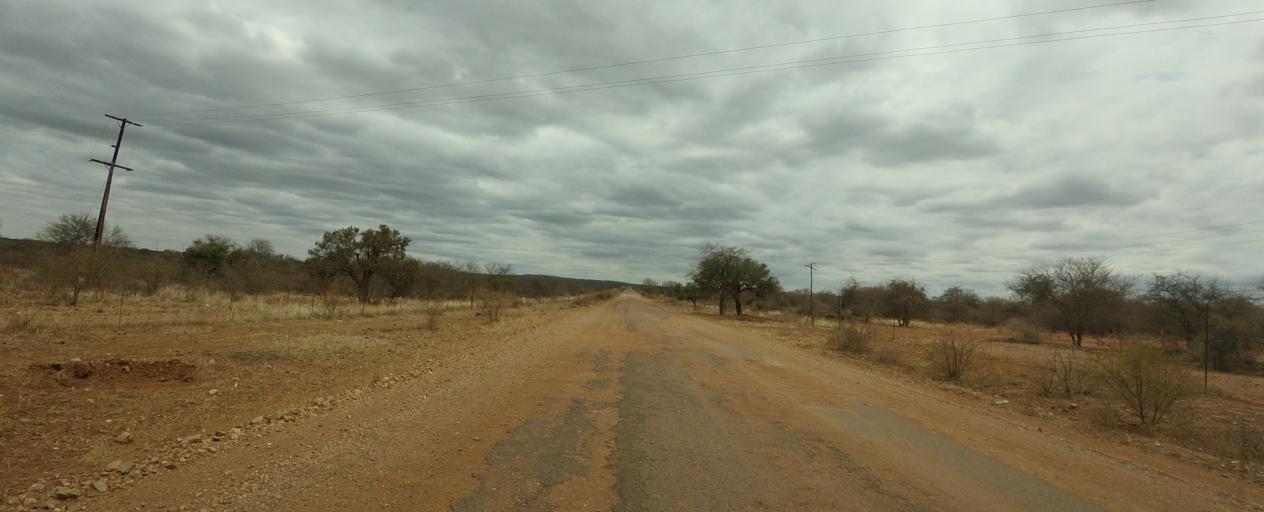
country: BW
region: Central
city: Mathathane
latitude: -22.7397
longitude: 28.4794
